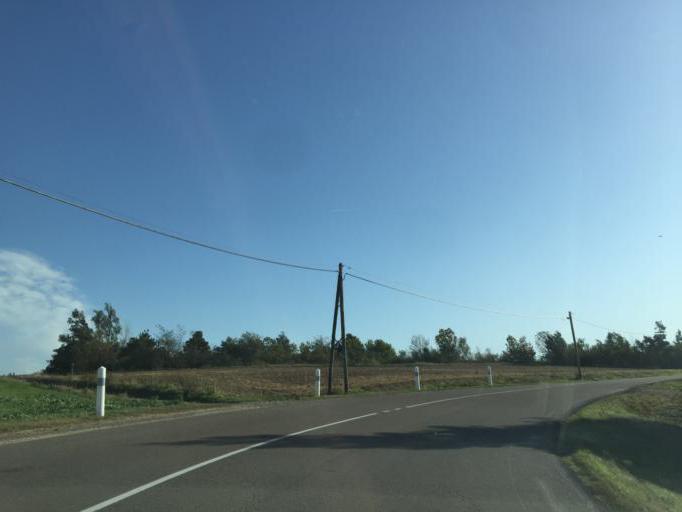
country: FR
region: Rhone-Alpes
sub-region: Departement de la Loire
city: Perigneux
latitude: 45.4600
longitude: 4.1102
